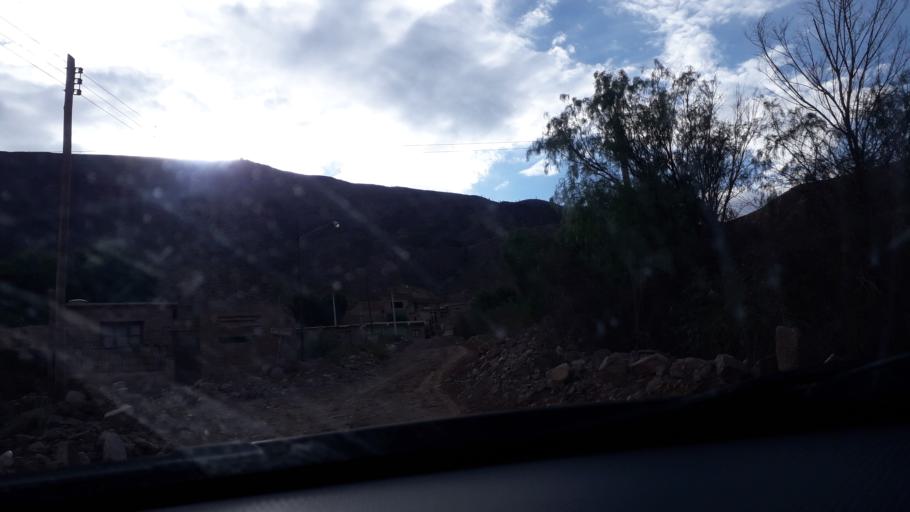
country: AR
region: Jujuy
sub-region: Departamento de Tilcara
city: Tilcara
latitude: -23.5807
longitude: -65.3869
